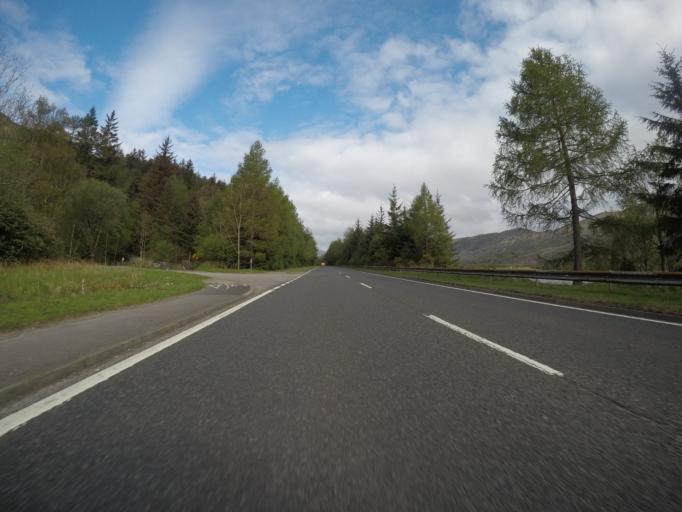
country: GB
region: Scotland
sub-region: Highland
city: Fort William
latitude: 56.6791
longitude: -5.1571
